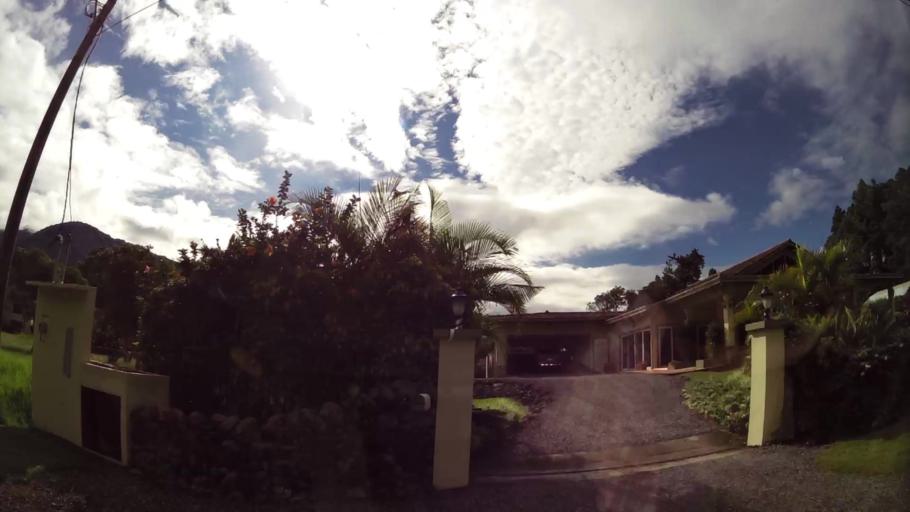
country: PA
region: Chiriqui
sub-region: Distrito Boquete
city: Boquete
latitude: 8.7989
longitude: -82.4330
